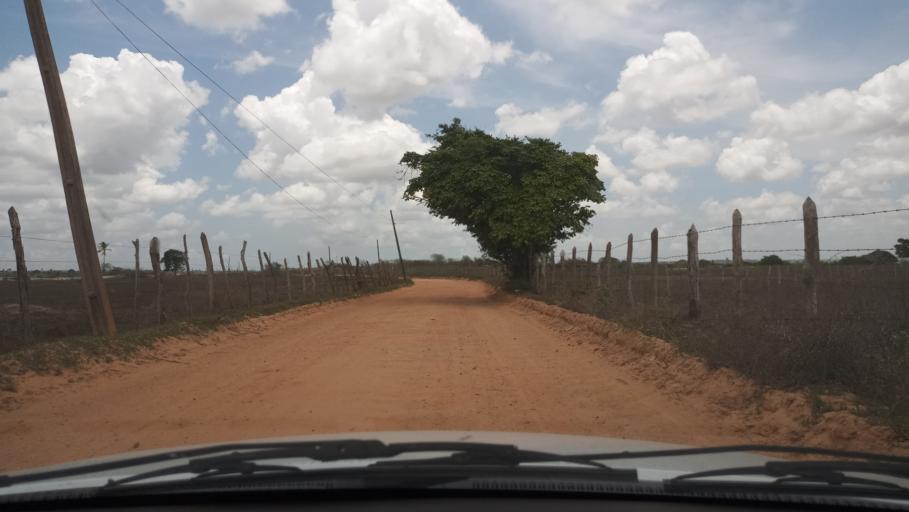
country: BR
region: Rio Grande do Norte
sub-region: Brejinho
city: Brejinho
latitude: -6.2823
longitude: -35.3400
